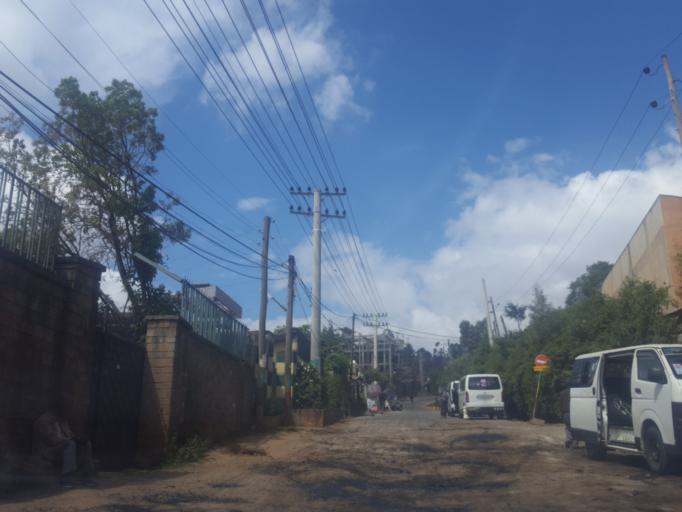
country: ET
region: Adis Abeba
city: Addis Ababa
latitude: 9.0634
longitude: 38.7436
